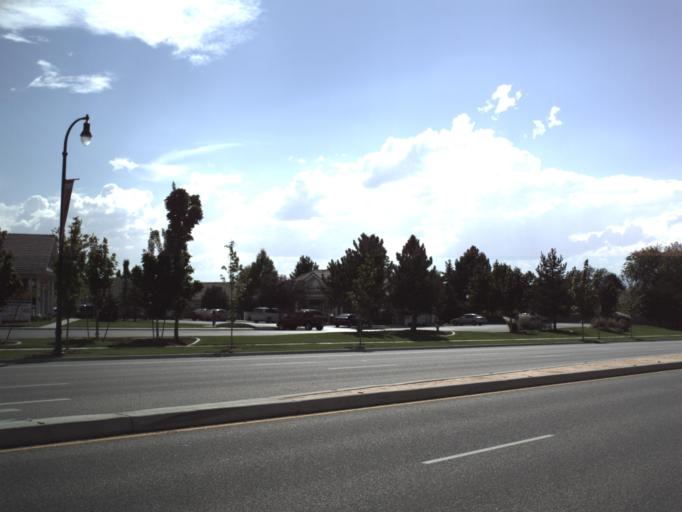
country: US
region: Utah
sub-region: Utah County
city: Orem
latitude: 40.3120
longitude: -111.6808
